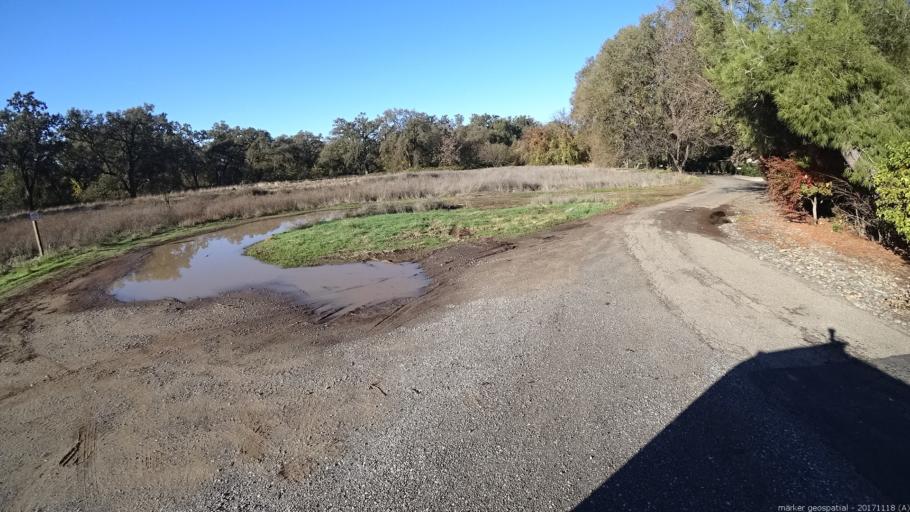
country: US
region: California
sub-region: Shasta County
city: Anderson
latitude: 40.4606
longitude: -122.2349
